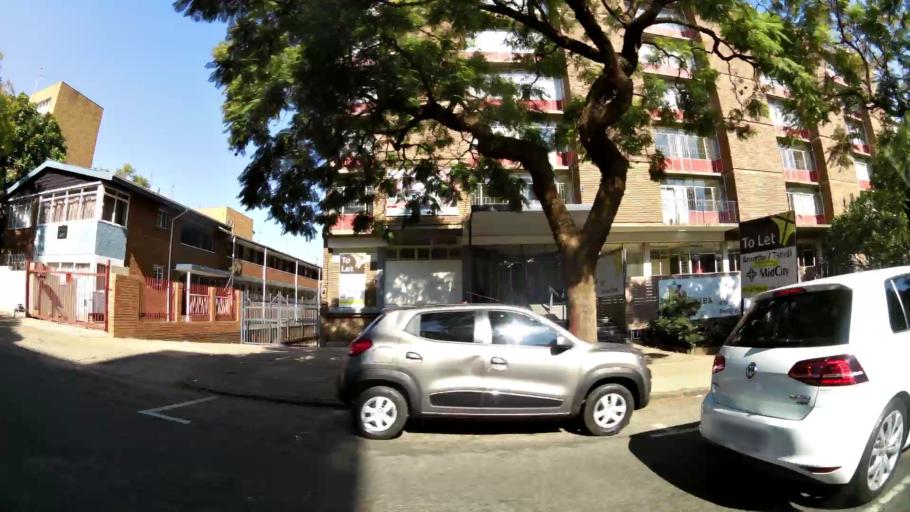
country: ZA
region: Gauteng
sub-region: City of Tshwane Metropolitan Municipality
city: Pretoria
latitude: -25.7462
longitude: 28.2134
